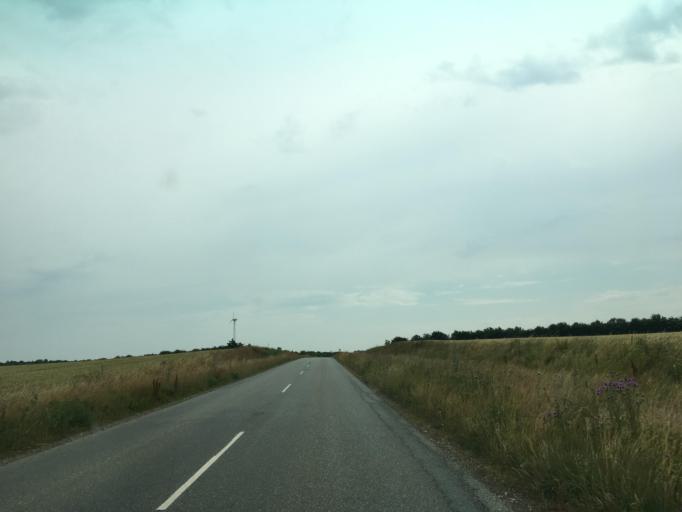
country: DK
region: North Denmark
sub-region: Thisted Kommune
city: Hurup
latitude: 56.7633
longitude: 8.4225
